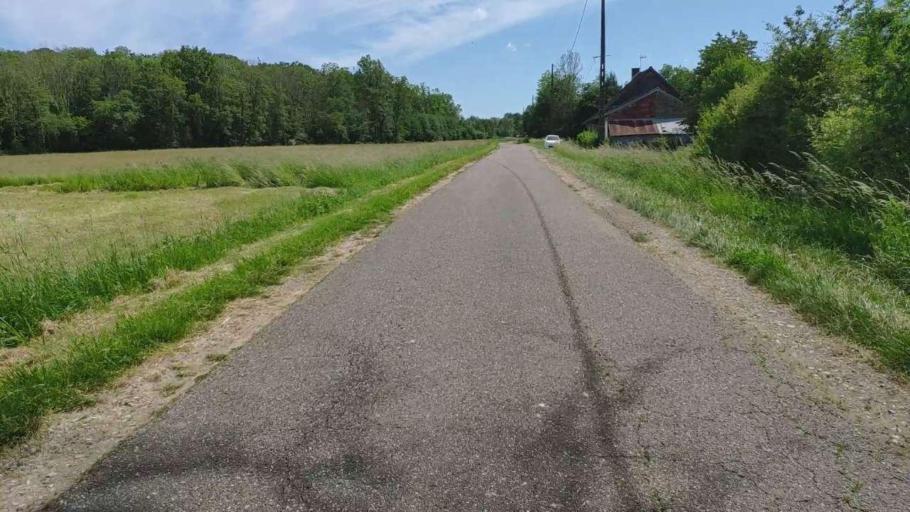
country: FR
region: Franche-Comte
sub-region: Departement du Jura
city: Bletterans
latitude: 46.7209
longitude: 5.4765
